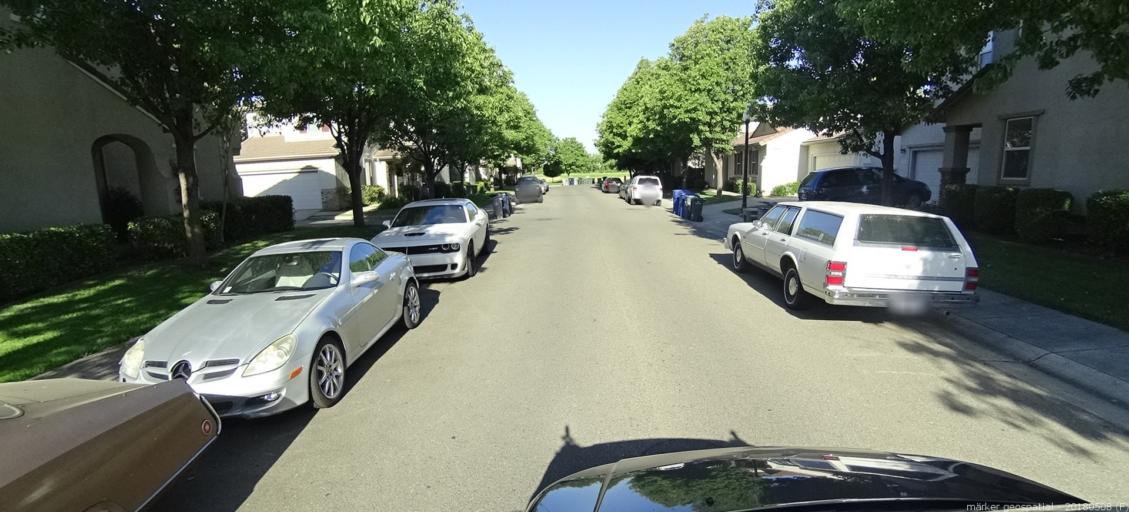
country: US
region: California
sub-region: Sacramento County
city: Elverta
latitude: 38.6725
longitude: -121.5057
